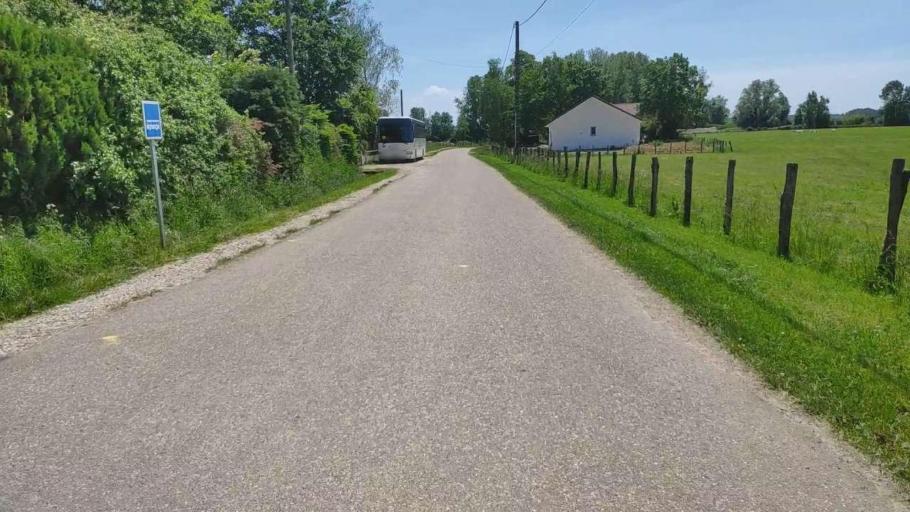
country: FR
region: Franche-Comte
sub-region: Departement du Jura
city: Bletterans
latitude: 46.7425
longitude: 5.4060
